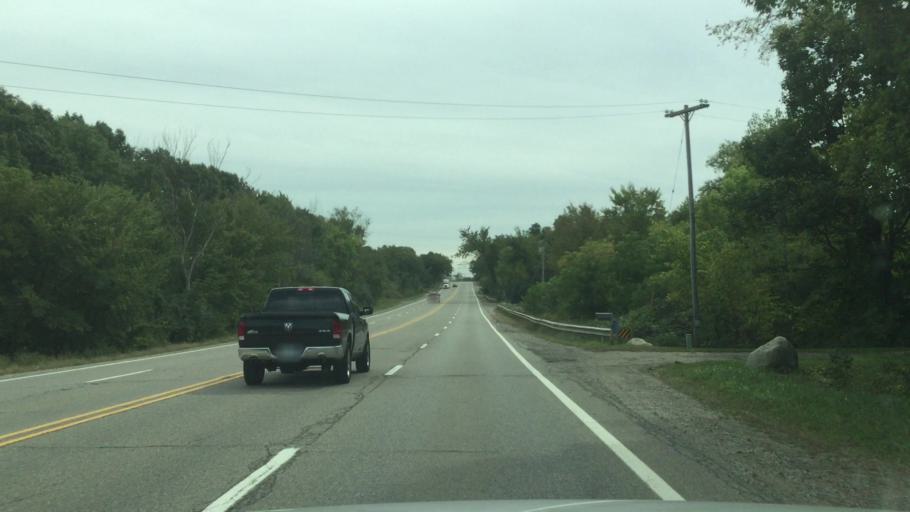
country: US
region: Michigan
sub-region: Oakland County
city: Ortonville
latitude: 42.7951
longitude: -83.5188
